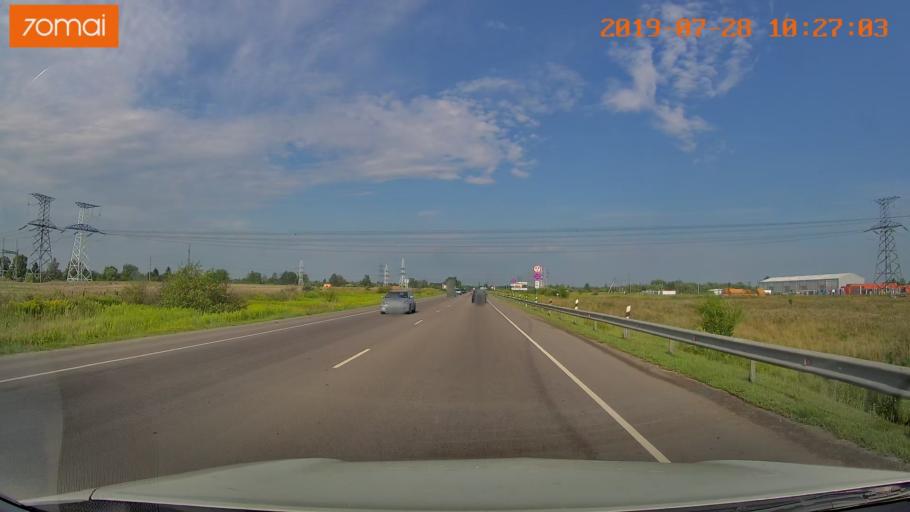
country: RU
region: Kaliningrad
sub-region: Gorod Kaliningrad
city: Kaliningrad
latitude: 54.7696
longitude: 20.5244
